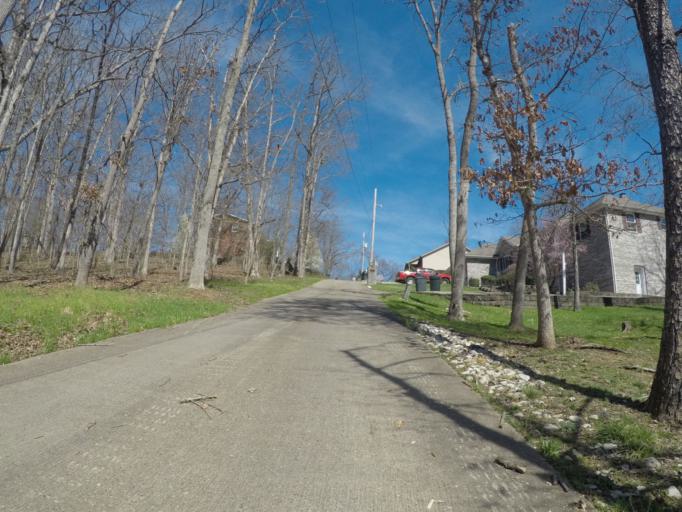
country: US
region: West Virginia
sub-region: Cabell County
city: Pea Ridge
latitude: 38.4019
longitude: -82.3373
